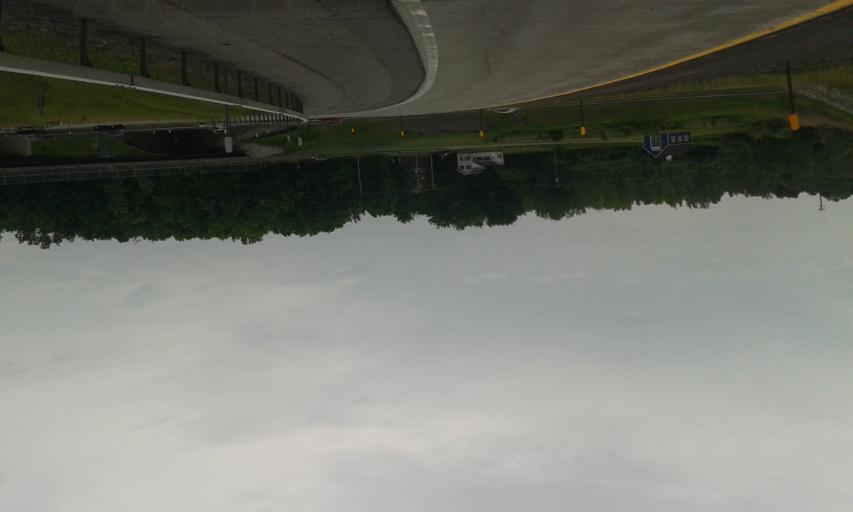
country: US
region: New York
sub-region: Onondaga County
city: Seneca Knolls
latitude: 43.1085
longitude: -76.2879
